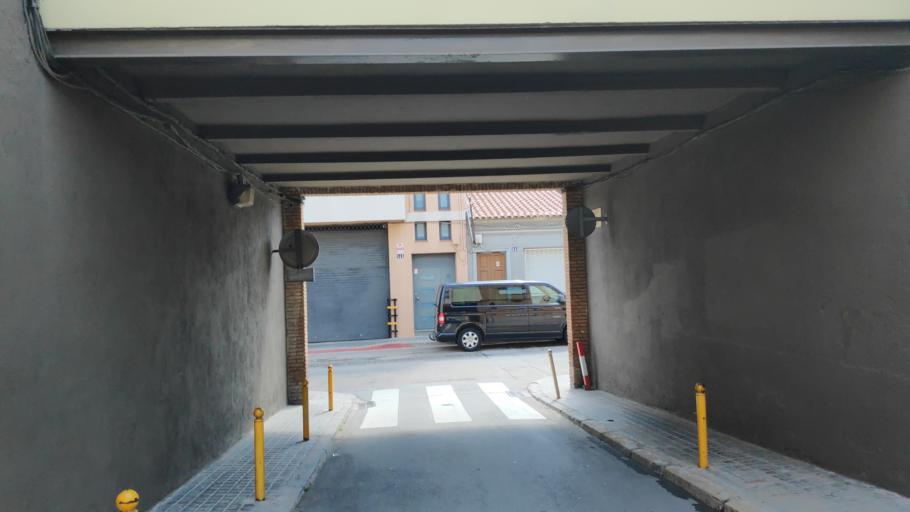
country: ES
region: Catalonia
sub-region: Provincia de Barcelona
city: Sabadell
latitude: 41.5382
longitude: 2.1004
